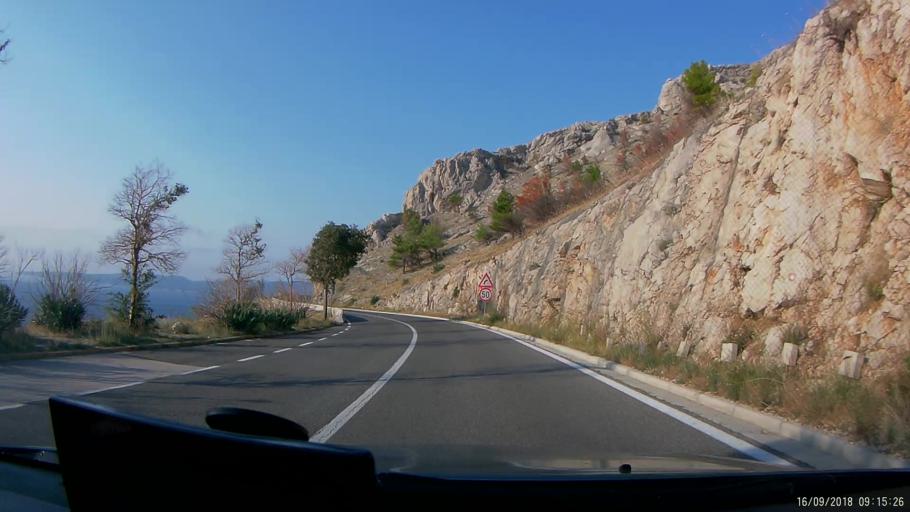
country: HR
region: Splitsko-Dalmatinska
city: Donja Brela
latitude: 43.4018
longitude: 16.8789
